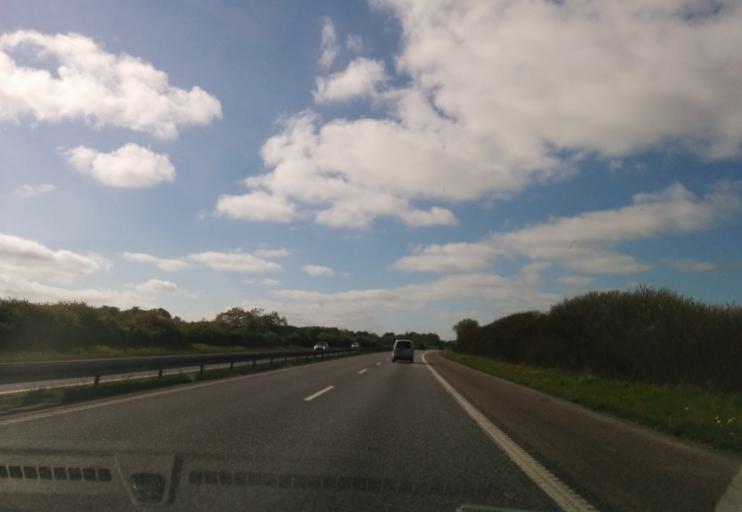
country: DK
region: South Denmark
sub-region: Fredericia Kommune
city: Taulov
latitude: 55.5928
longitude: 9.5976
